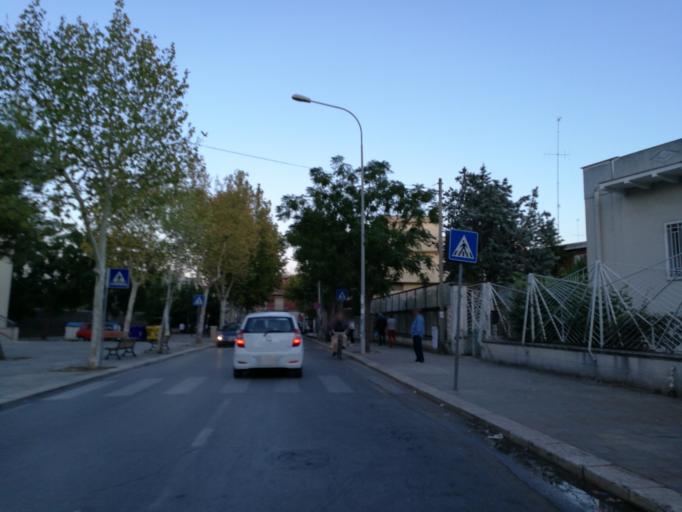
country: IT
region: Apulia
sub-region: Provincia di Bari
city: Valenzano
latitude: 41.0659
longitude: 16.8672
